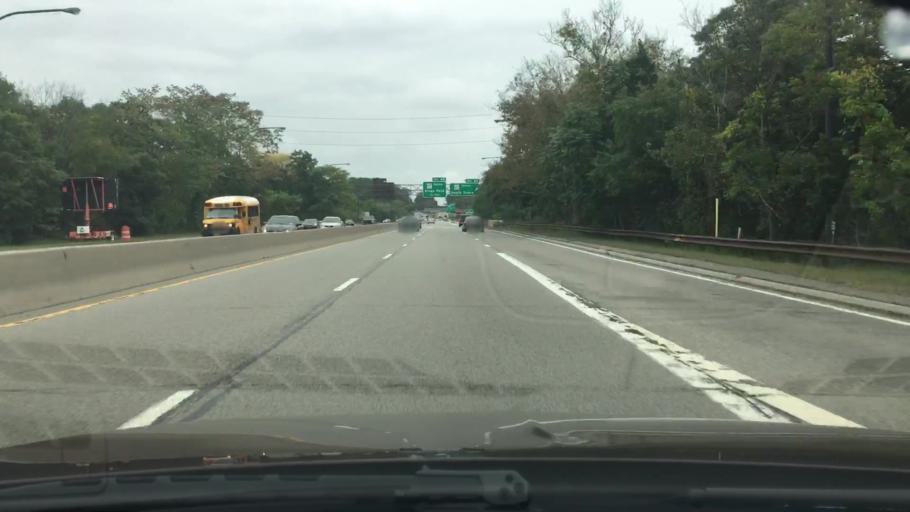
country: US
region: New York
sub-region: Suffolk County
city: Commack
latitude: 40.8186
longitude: -73.2951
